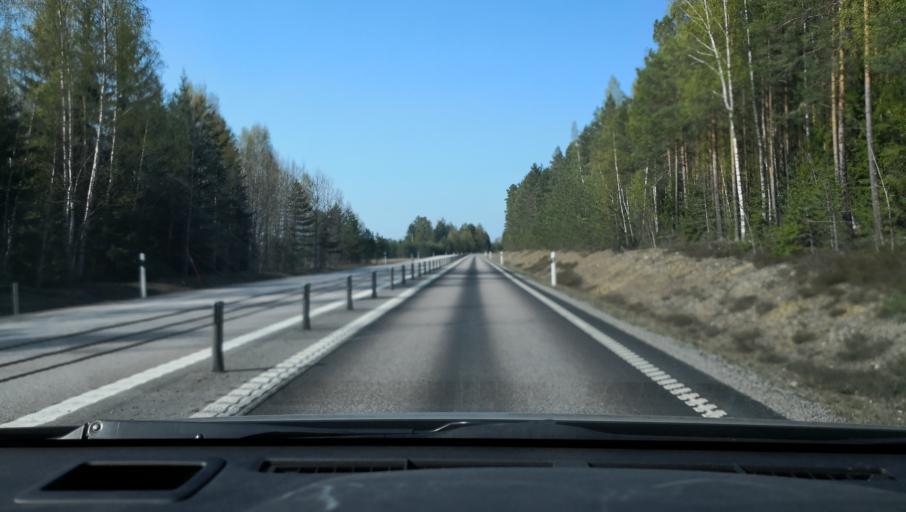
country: SE
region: Uppsala
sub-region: Heby Kommun
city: Tarnsjo
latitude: 60.2165
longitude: 16.9522
